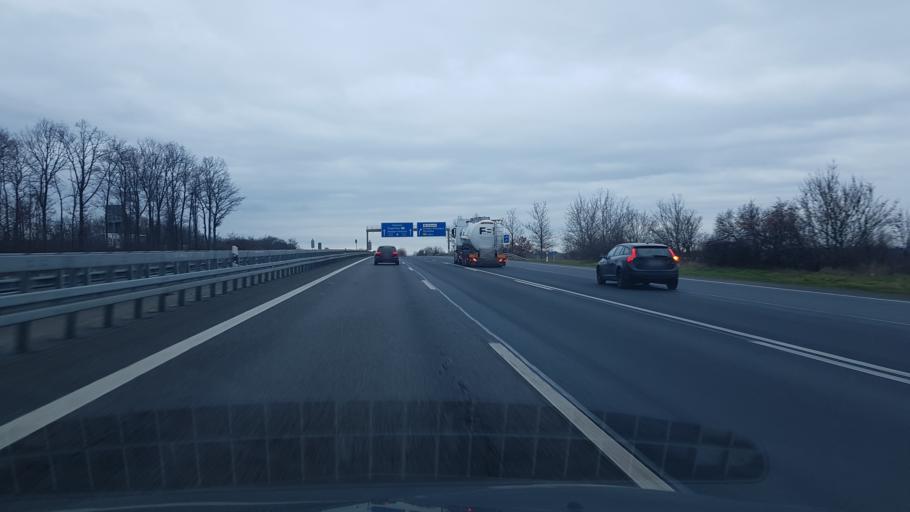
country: DE
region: Saxony
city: Albertstadt
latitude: 51.1297
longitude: 13.7459
